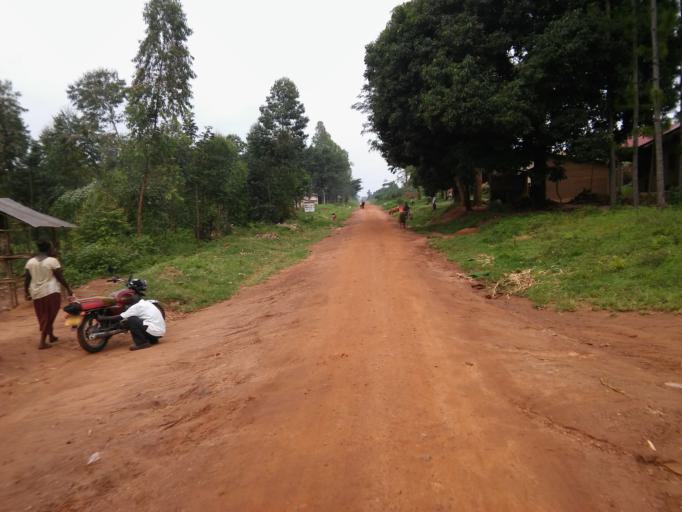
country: UG
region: Eastern Region
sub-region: Mbale District
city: Mbale
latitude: 0.9948
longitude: 34.1959
